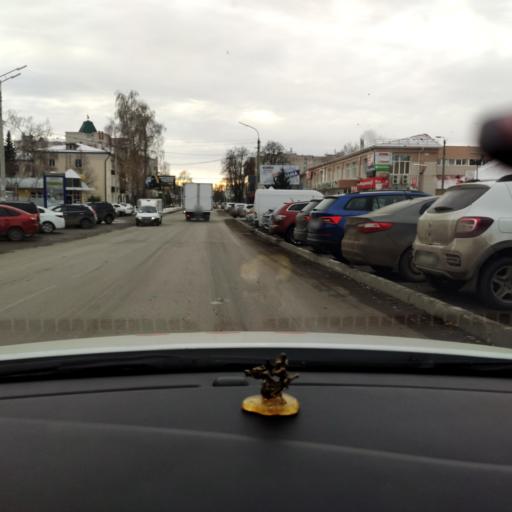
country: RU
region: Tatarstan
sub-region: Zelenodol'skiy Rayon
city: Zelenodolsk
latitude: 55.8501
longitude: 48.5018
